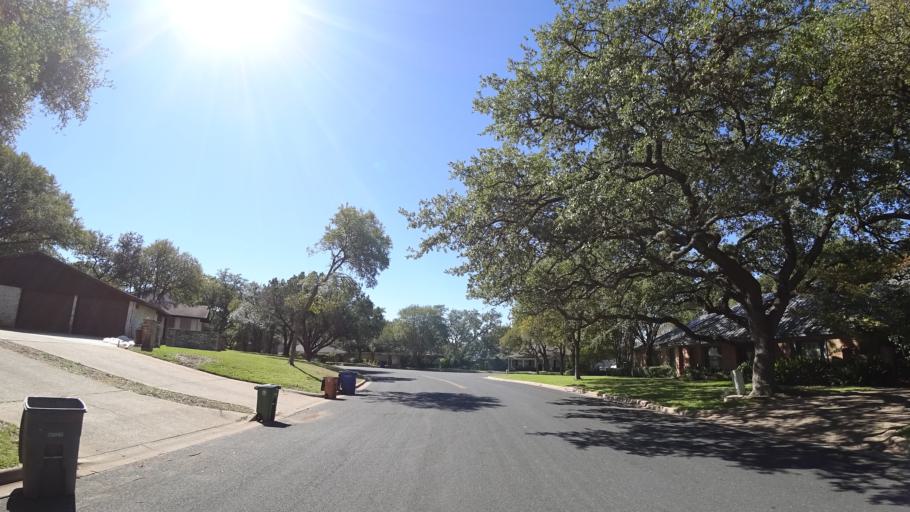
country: US
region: Texas
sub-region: Travis County
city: West Lake Hills
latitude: 30.3637
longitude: -97.7704
